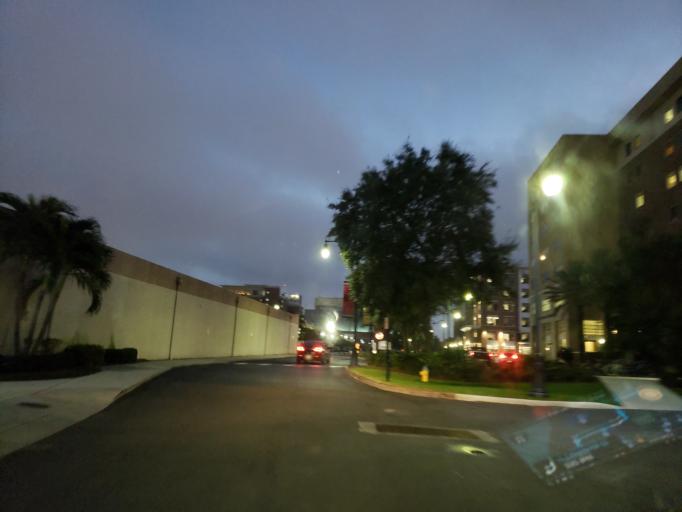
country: US
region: Florida
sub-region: Hillsborough County
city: Tampa
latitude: 27.9490
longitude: -82.4664
